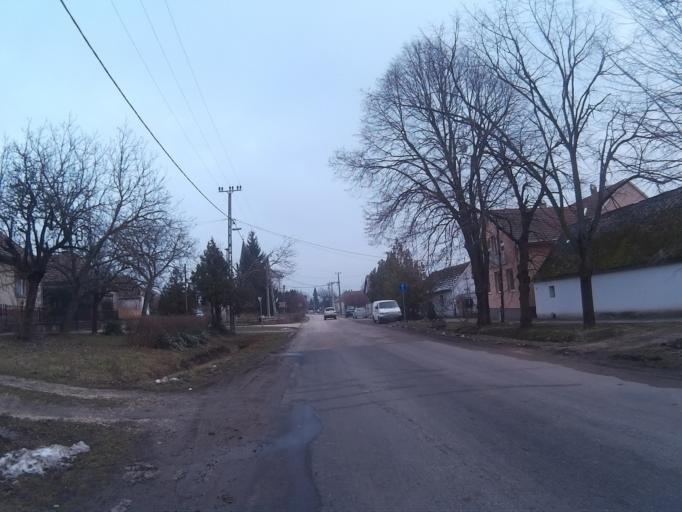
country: HU
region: Komarom-Esztergom
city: Tarjan
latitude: 47.6473
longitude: 18.5097
